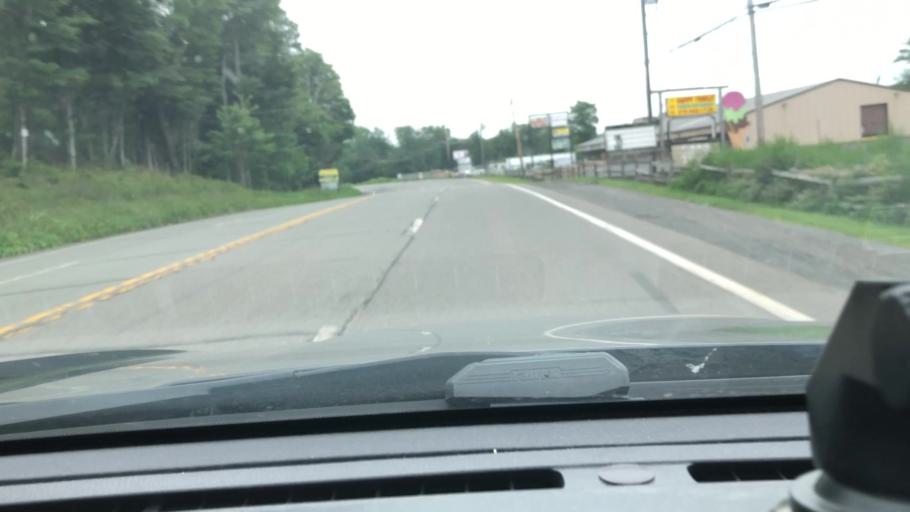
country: US
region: Pennsylvania
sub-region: Lackawanna County
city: Moscow
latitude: 41.2488
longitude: -75.5029
